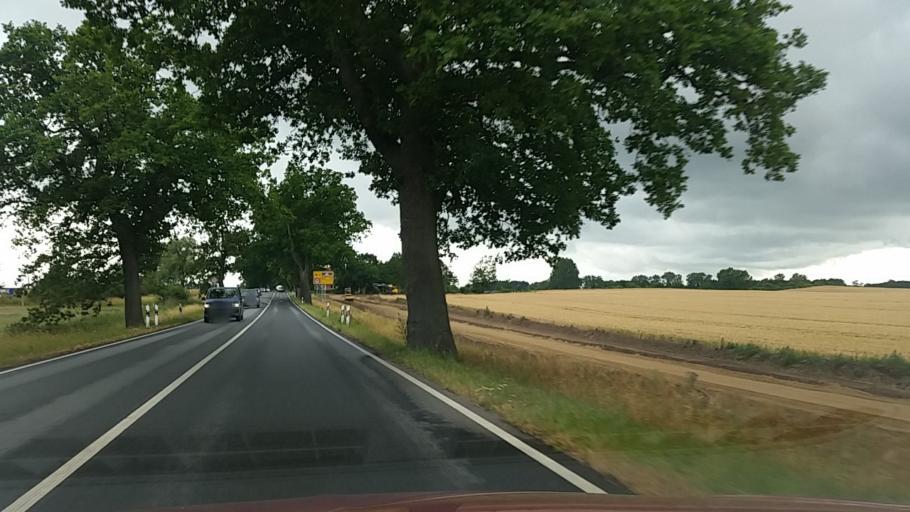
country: DE
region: Mecklenburg-Vorpommern
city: Sellin
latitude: 53.9129
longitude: 11.5797
